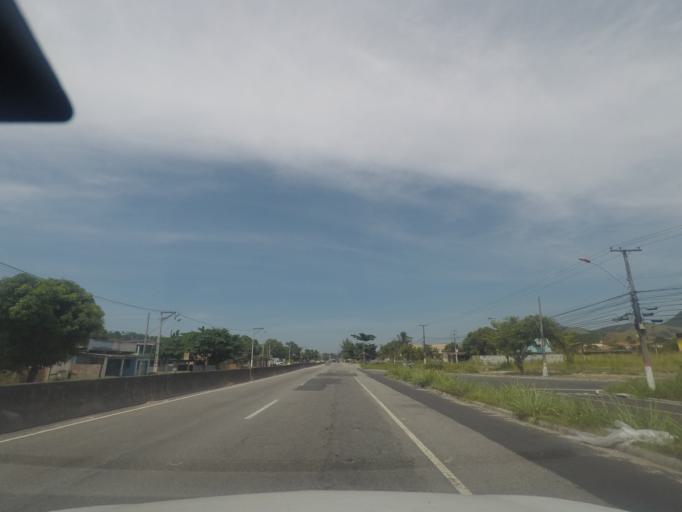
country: BR
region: Rio de Janeiro
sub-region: Marica
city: Marica
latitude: -22.9242
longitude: -42.8625
